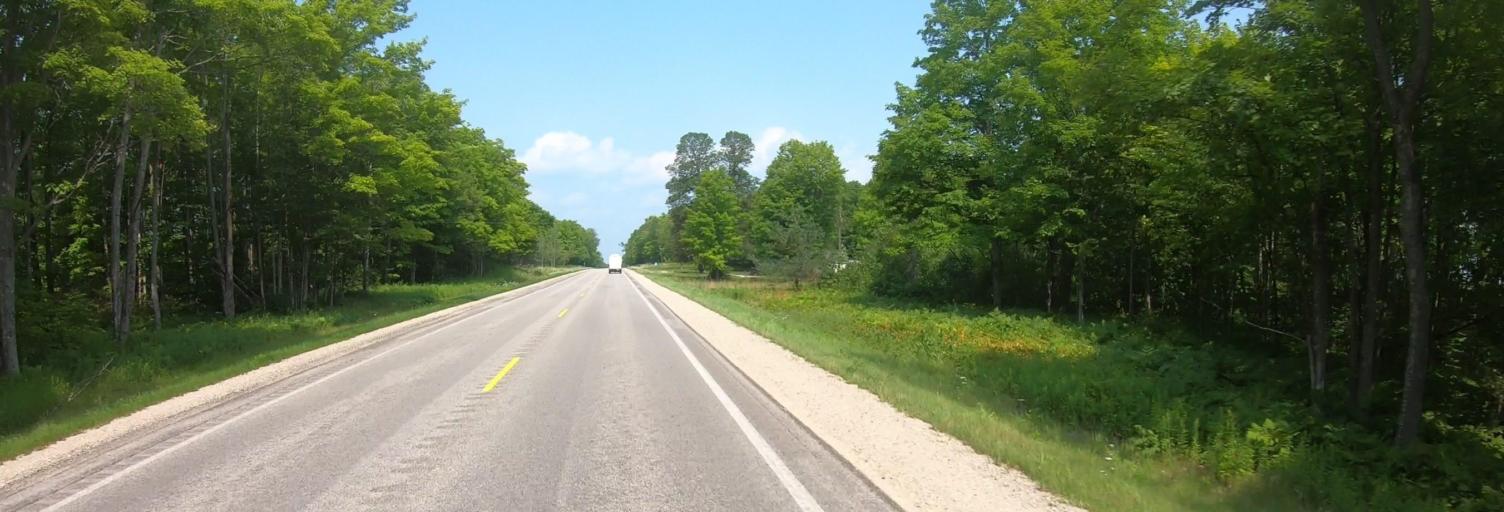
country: US
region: Michigan
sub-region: Luce County
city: Newberry
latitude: 46.3185
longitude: -85.6658
